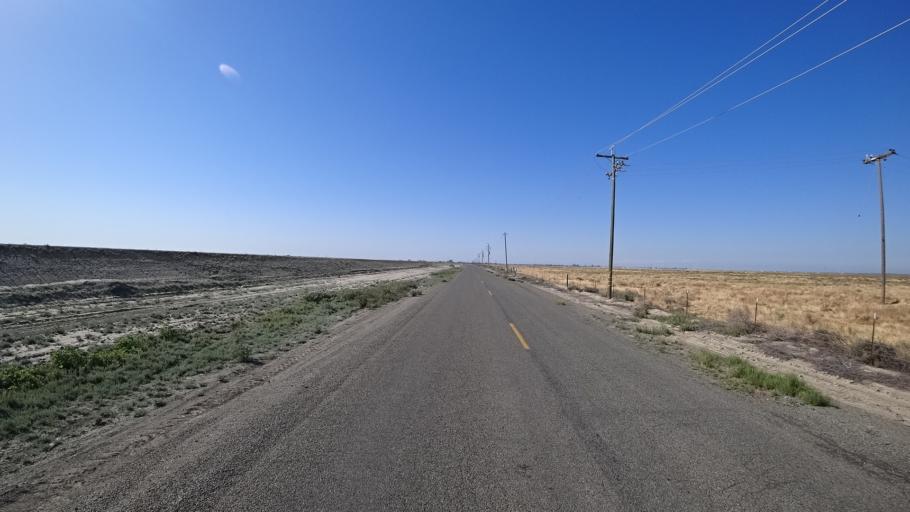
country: US
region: California
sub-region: Kings County
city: Corcoran
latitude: 36.1519
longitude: -119.5649
